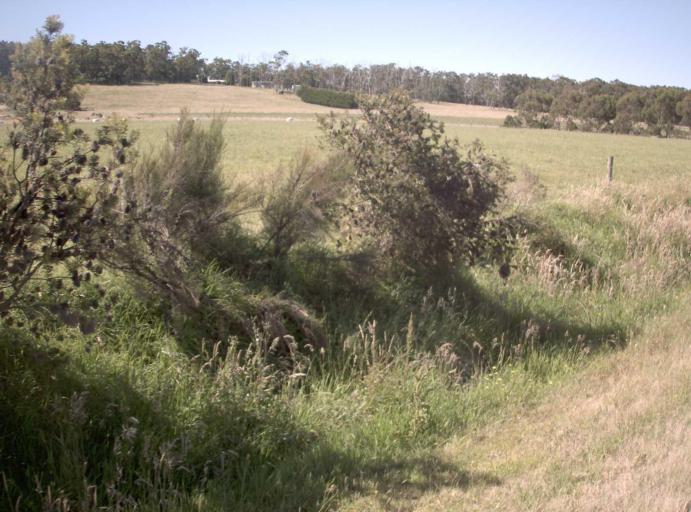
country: AU
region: Victoria
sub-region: Latrobe
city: Morwell
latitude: -38.6494
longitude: 146.4692
